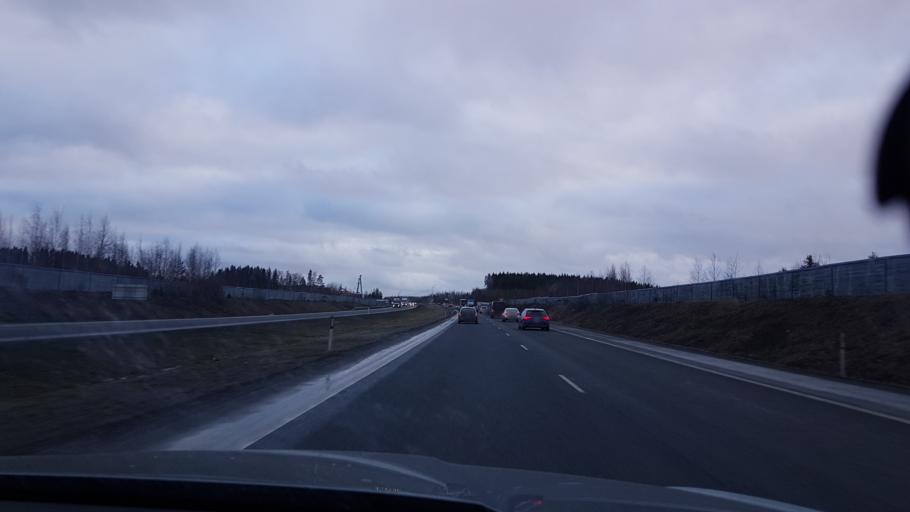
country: FI
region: Pirkanmaa
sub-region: Tampere
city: Lempaeaelae
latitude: 61.3773
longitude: 23.7907
